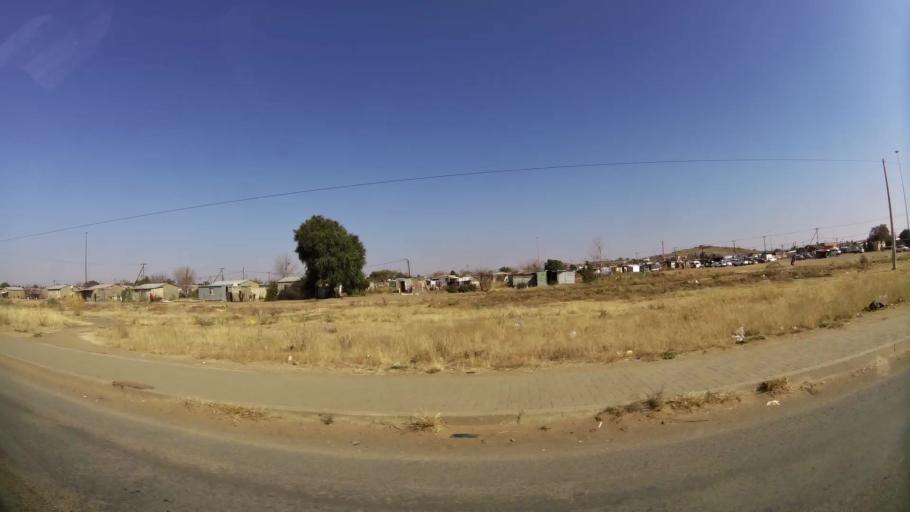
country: ZA
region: Orange Free State
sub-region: Mangaung Metropolitan Municipality
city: Bloemfontein
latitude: -29.1701
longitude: 26.2611
